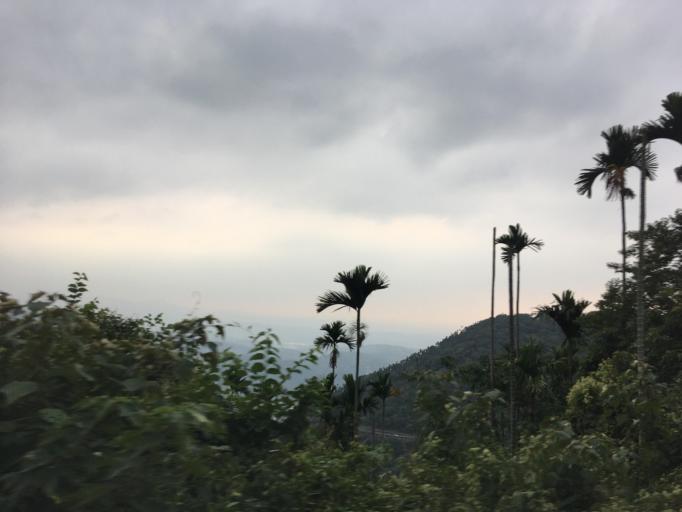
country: TW
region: Taiwan
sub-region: Chiayi
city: Jiayi Shi
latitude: 23.5339
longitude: 120.6065
